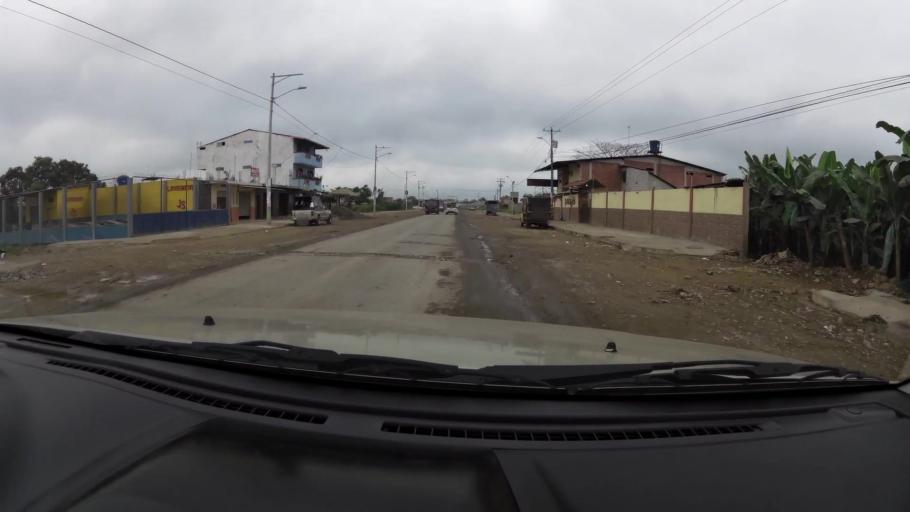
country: EC
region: El Oro
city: Pasaje
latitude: -3.3396
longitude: -79.8147
